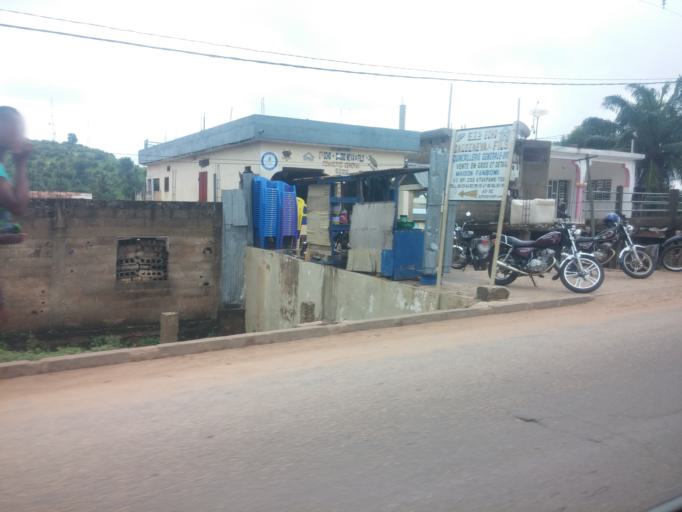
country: TG
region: Plateaux
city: Atakpame
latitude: 7.5167
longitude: 1.1485
